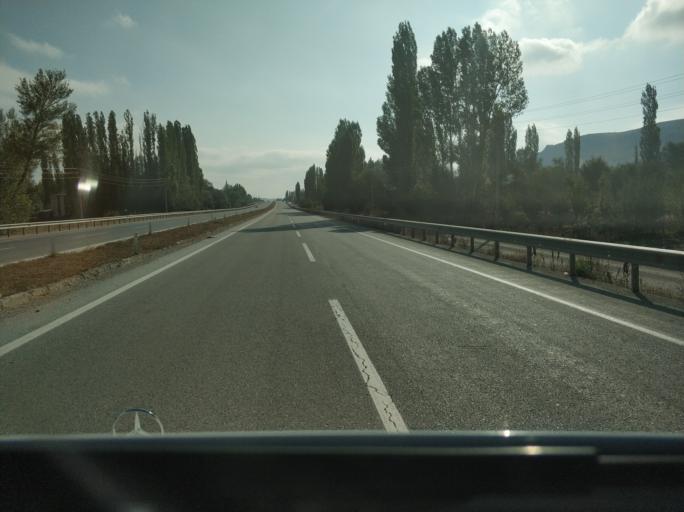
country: TR
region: Sivas
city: Yildizeli
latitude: 39.8404
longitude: 36.4634
